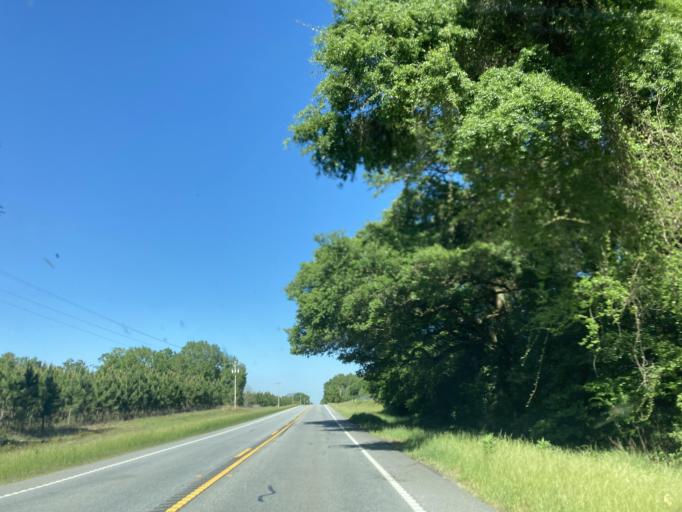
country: US
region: Georgia
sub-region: Baker County
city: Newton
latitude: 31.2740
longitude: -84.3849
